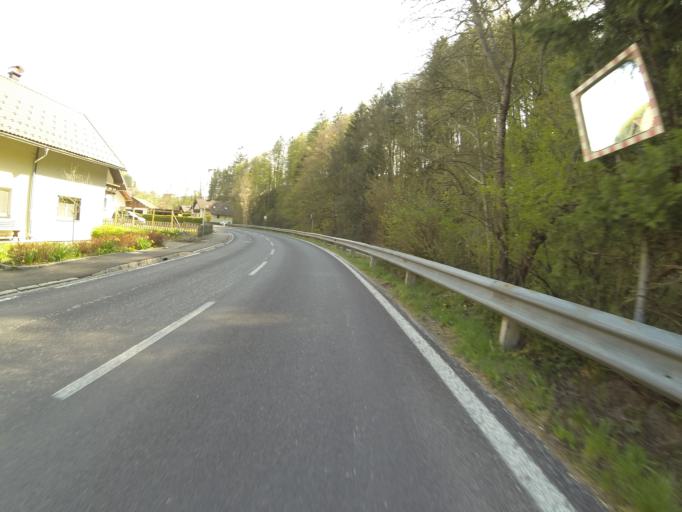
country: AT
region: Upper Austria
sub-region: Politischer Bezirk Gmunden
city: Altmunster
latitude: 47.9055
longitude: 13.7092
